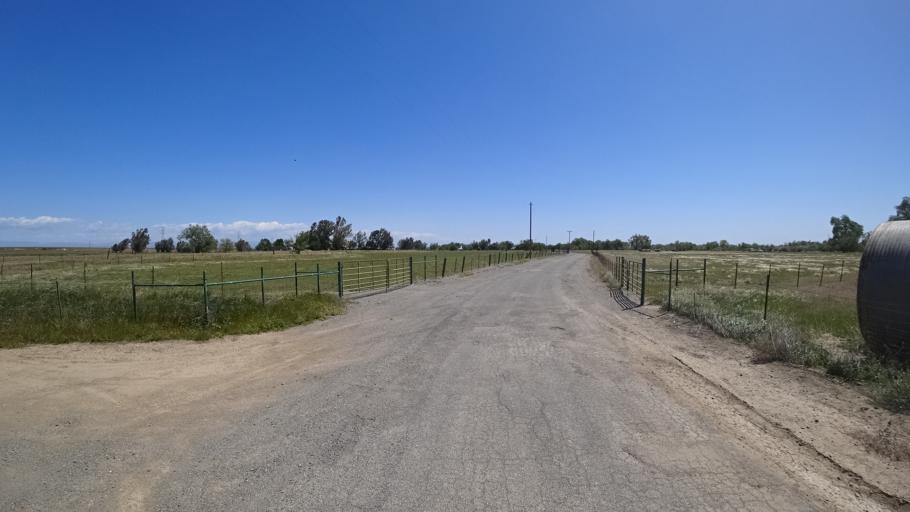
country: US
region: California
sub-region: Glenn County
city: Orland
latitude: 39.7980
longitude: -122.2564
